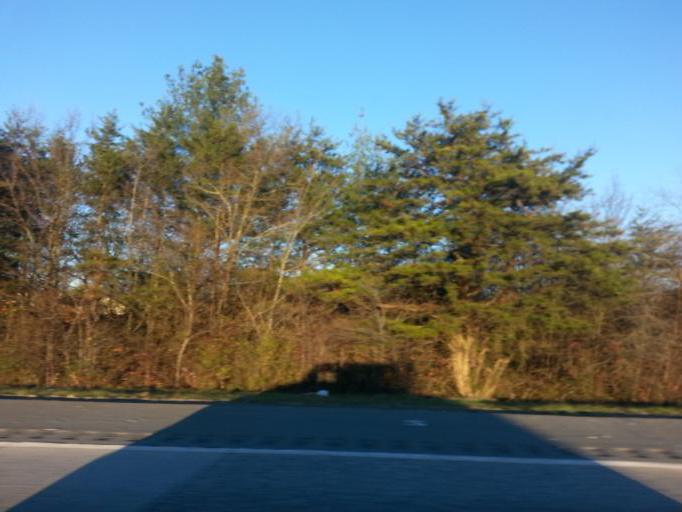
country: US
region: North Carolina
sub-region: Henderson County
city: Fletcher
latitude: 35.4104
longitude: -82.5185
